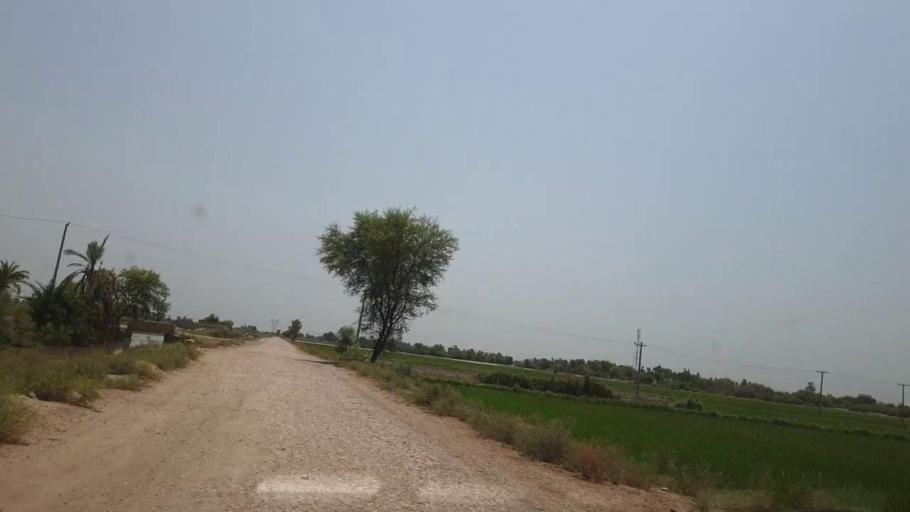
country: PK
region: Sindh
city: Lakhi
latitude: 27.8649
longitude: 68.6065
